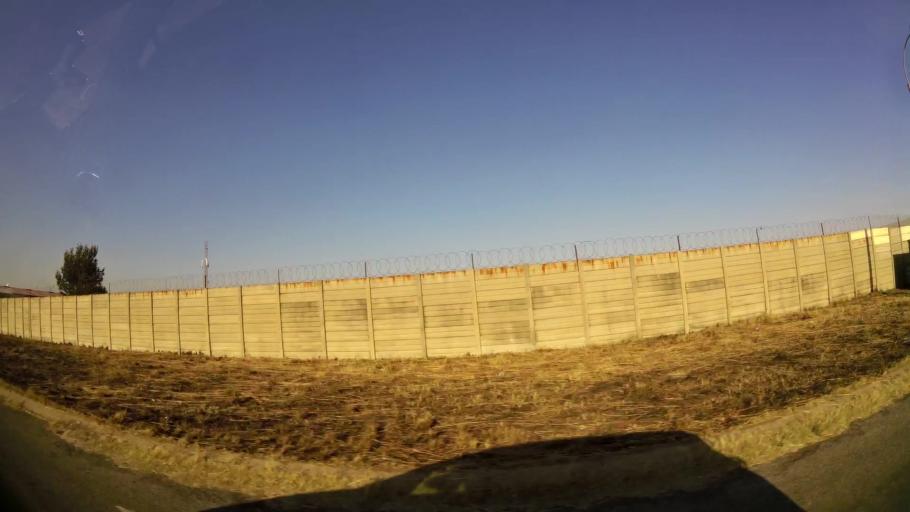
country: ZA
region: Gauteng
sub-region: West Rand District Municipality
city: Randfontein
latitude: -26.1990
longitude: 27.6897
